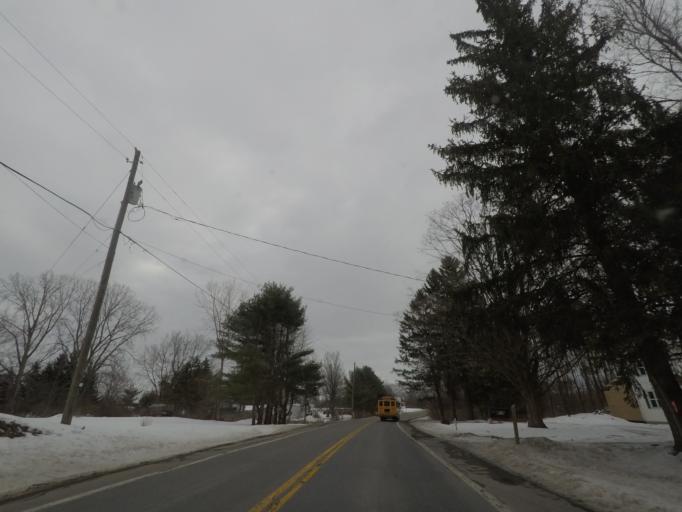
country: US
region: New York
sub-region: Saratoga County
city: Stillwater
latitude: 42.9668
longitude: -73.6802
